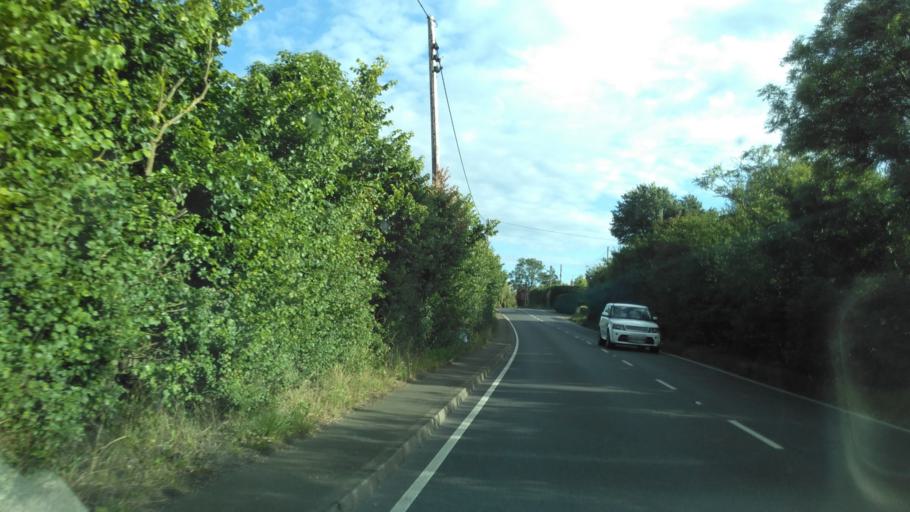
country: GB
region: England
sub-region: Kent
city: Whitstable
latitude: 51.3314
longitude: 1.0242
